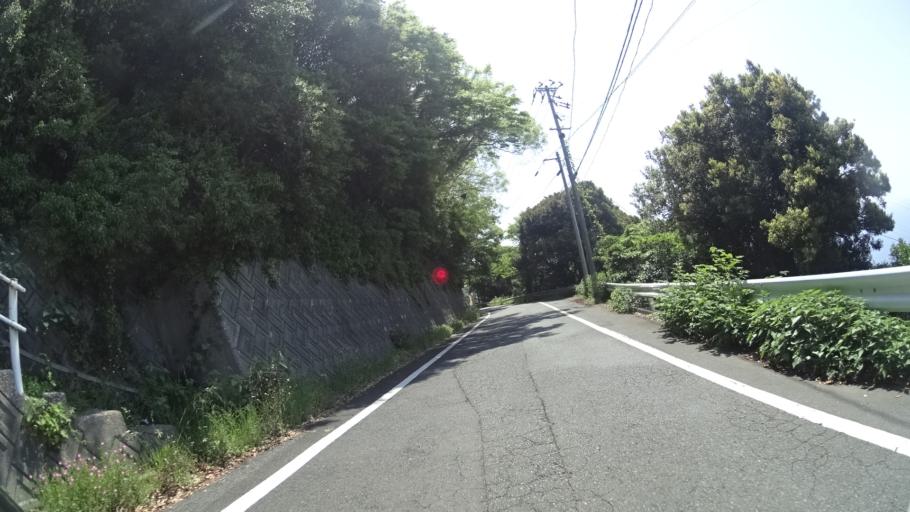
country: JP
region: Ehime
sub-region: Nishiuwa-gun
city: Ikata-cho
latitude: 33.3836
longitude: 132.0807
